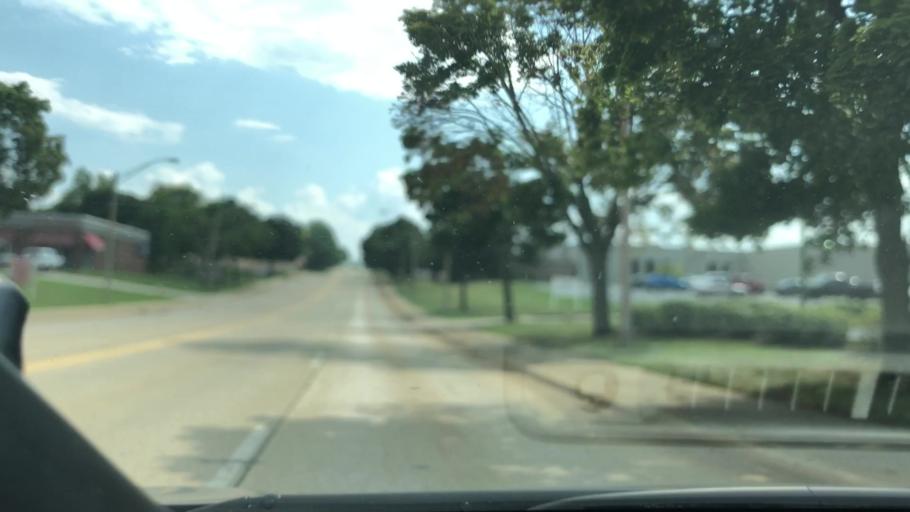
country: US
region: Ohio
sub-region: Summit County
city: Akron
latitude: 41.0698
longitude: -81.5205
